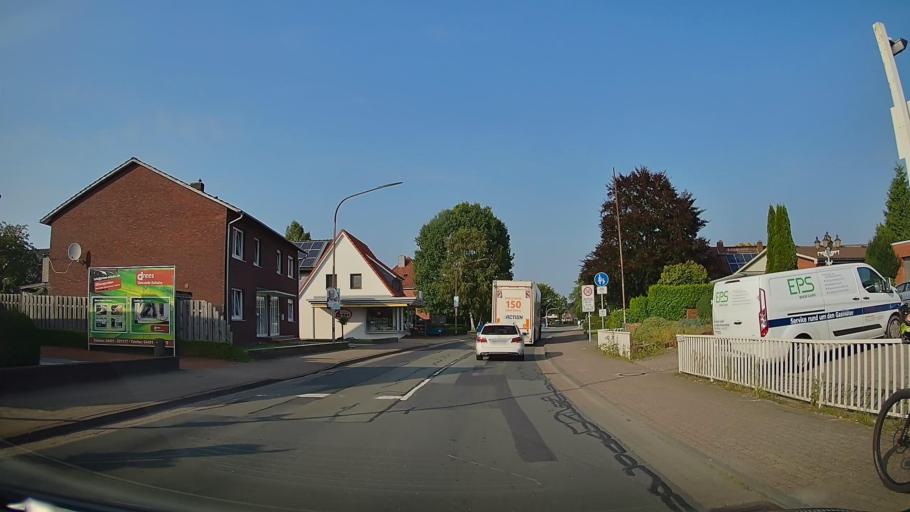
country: DE
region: Lower Saxony
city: Friesoythe
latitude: 53.0259
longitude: 7.8551
